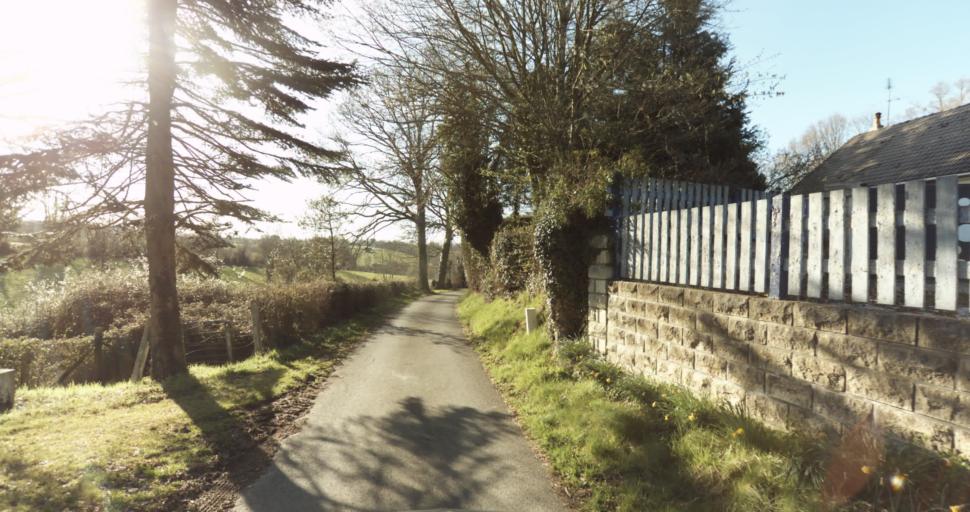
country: FR
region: Lower Normandy
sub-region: Departement du Calvados
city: Livarot
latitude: 48.9922
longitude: 0.1013
